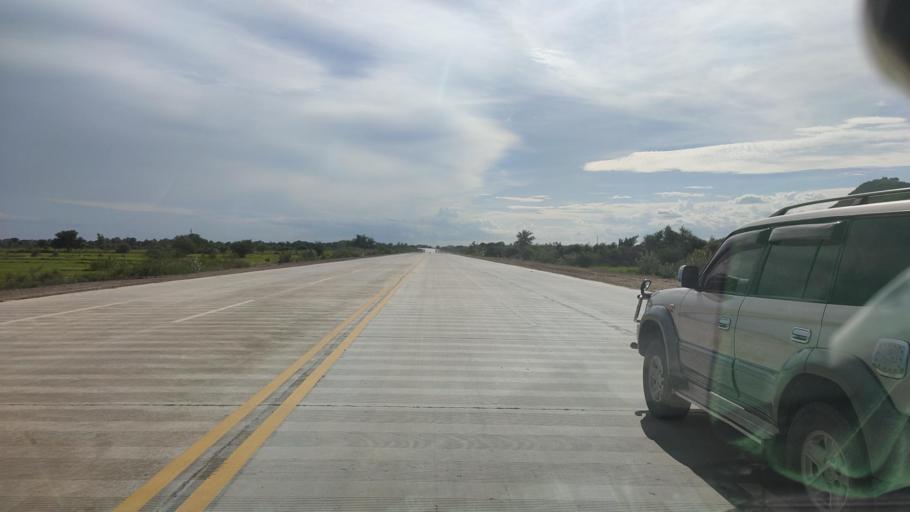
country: MM
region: Mandalay
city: Kyaukse
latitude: 21.5962
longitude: 96.1647
